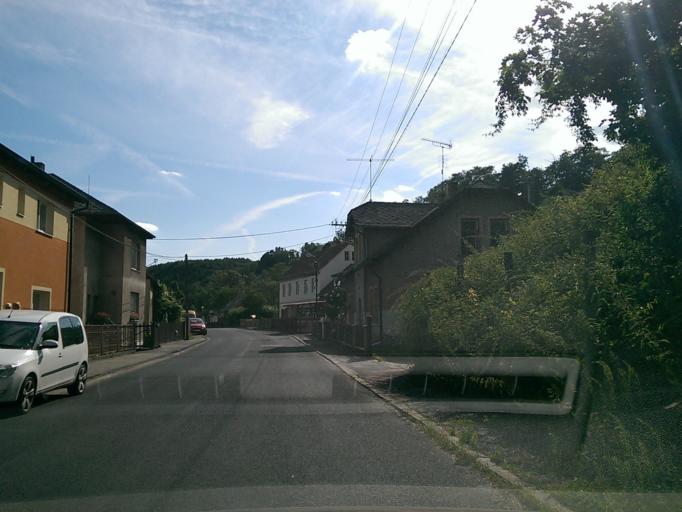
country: CZ
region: Central Bohemia
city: Bakov nad Jizerou
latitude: 50.4705
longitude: 14.9212
